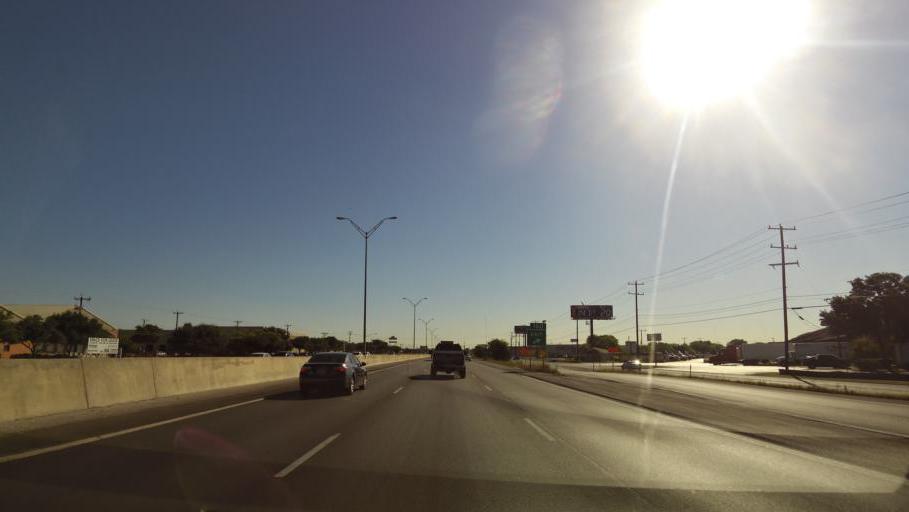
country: US
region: Texas
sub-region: Bexar County
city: Terrell Hills
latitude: 29.4432
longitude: -98.4357
